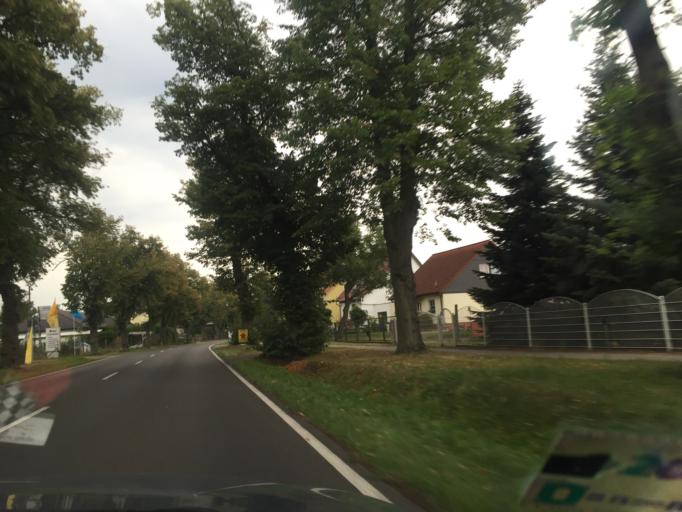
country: DE
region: Brandenburg
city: Wandlitz
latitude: 52.7556
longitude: 13.3824
